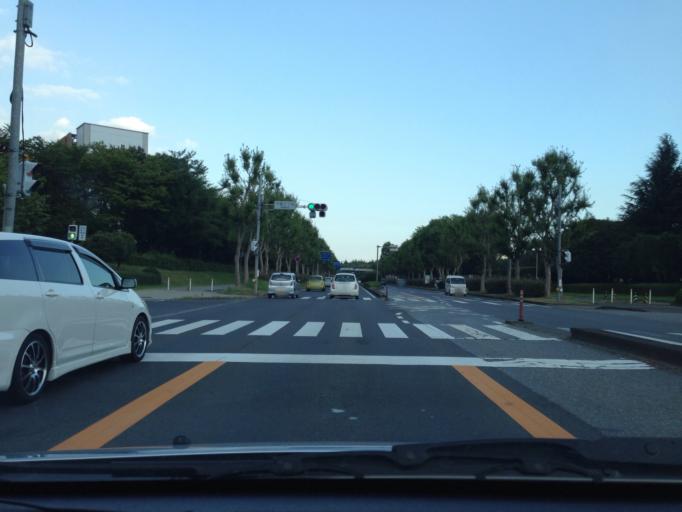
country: JP
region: Ibaraki
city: Naka
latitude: 36.0695
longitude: 140.1299
